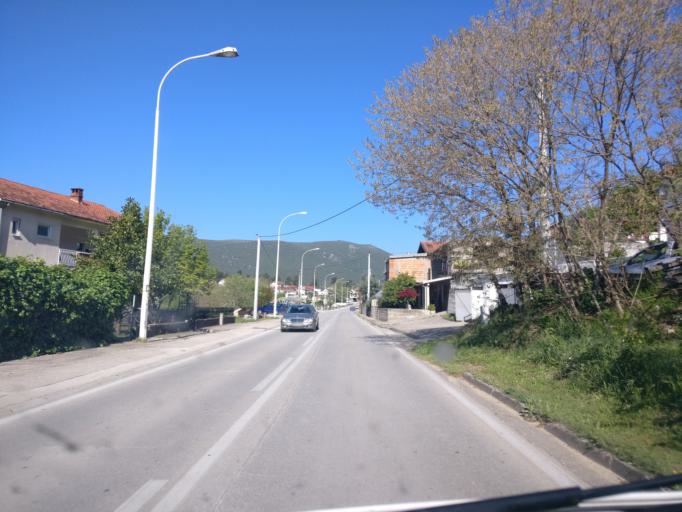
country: BA
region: Federation of Bosnia and Herzegovina
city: Capljina
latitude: 43.1182
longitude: 17.6934
